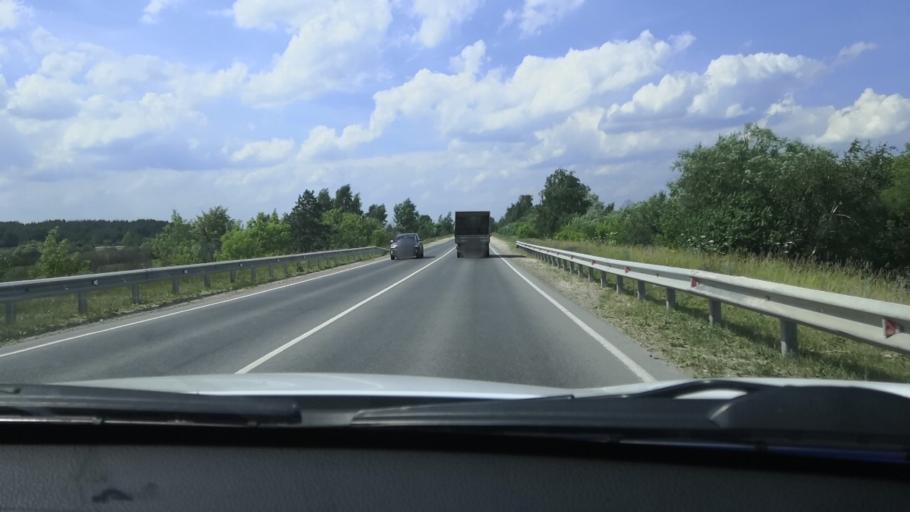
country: RU
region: Rjazan
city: Murmino
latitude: 54.6338
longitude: 39.9490
